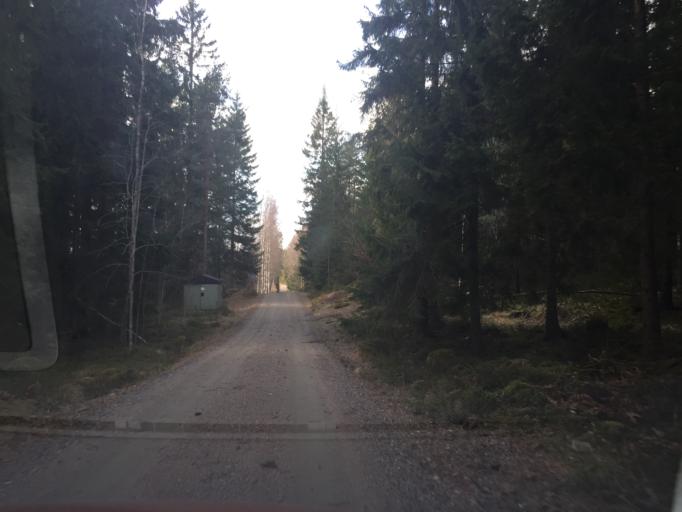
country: SE
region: Soedermanland
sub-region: Vingakers Kommun
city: Vingaker
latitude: 58.9900
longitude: 15.6897
